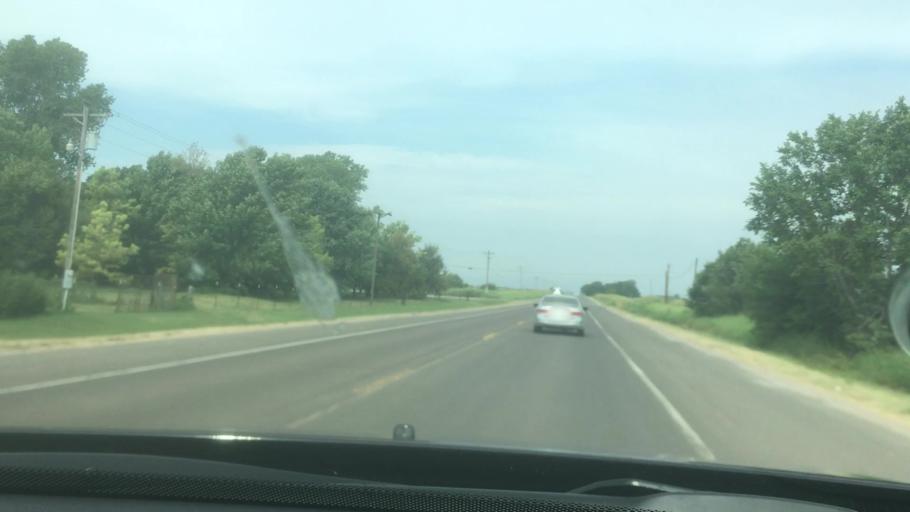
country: US
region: Oklahoma
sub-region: Garvin County
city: Maysville
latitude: 34.8192
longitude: -97.4557
